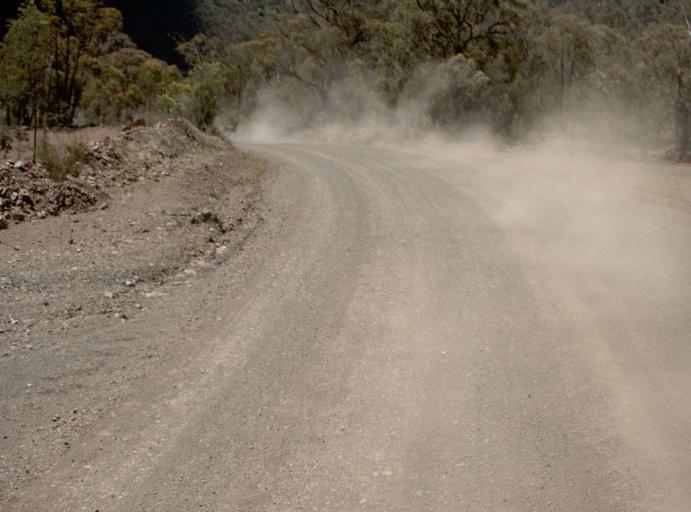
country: AU
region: New South Wales
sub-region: Bombala
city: Bombala
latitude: -37.1020
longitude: 148.6361
